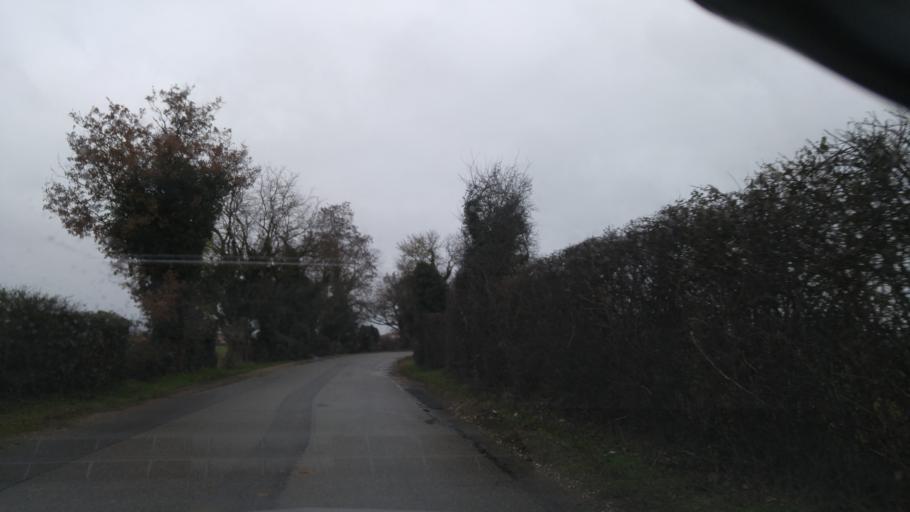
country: FR
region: Rhone-Alpes
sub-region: Departement du Rhone
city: Saint-Laurent-de-Mure
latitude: 45.6973
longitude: 5.0404
